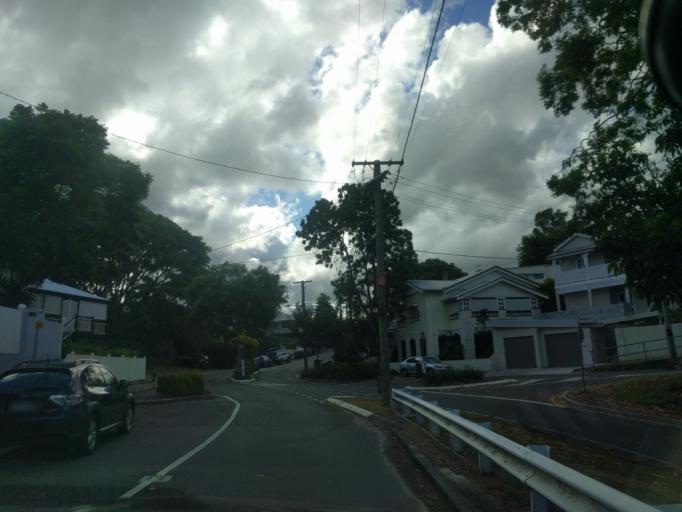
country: AU
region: Queensland
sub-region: Brisbane
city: Fortitude Valley
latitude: -27.4596
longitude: 153.0466
